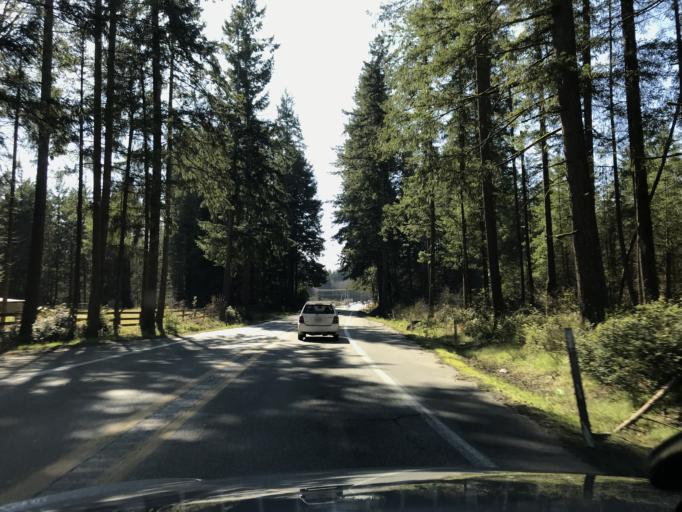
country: US
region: Washington
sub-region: Pierce County
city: Wauna
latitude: 47.3840
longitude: -122.6900
